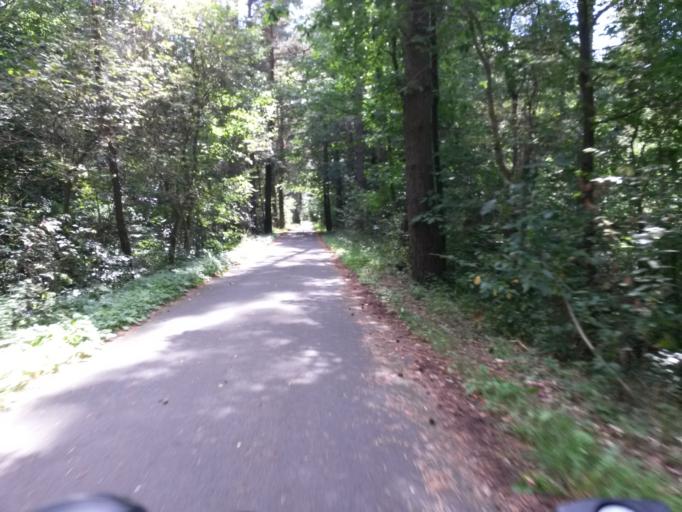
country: DE
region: Brandenburg
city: Templin
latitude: 53.1713
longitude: 13.5175
